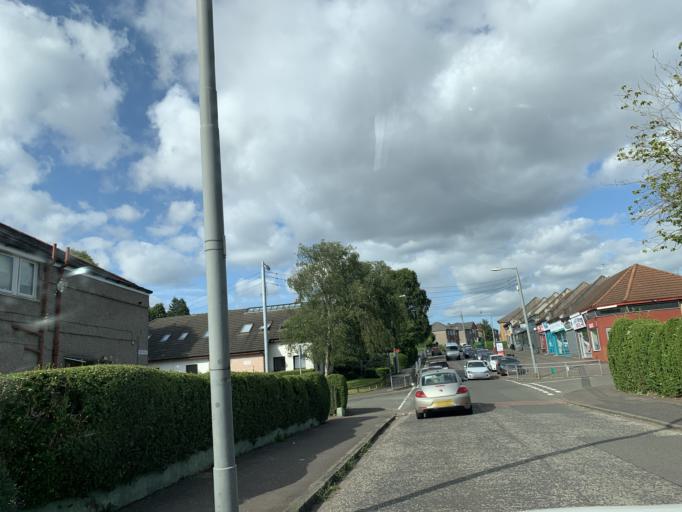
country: GB
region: Scotland
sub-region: Renfrewshire
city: Renfrew
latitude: 55.8503
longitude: -4.3583
